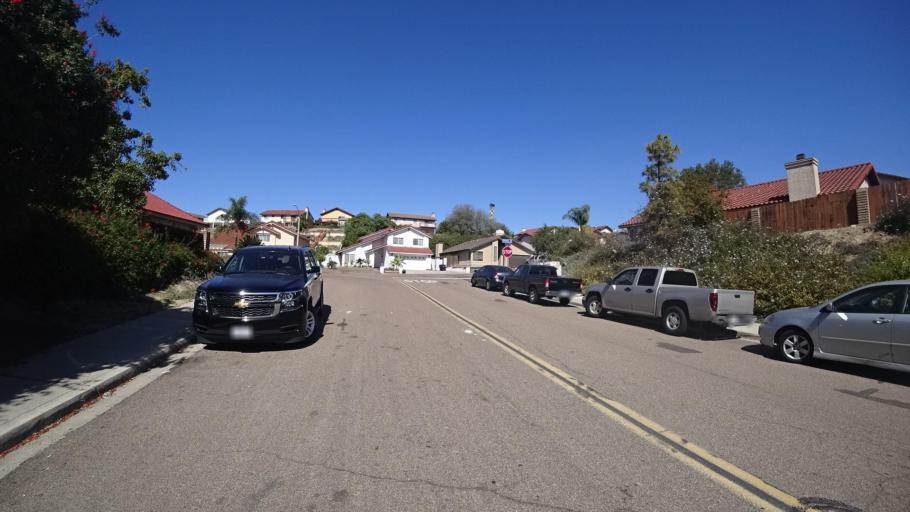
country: US
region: California
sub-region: San Diego County
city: Bonita
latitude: 32.6430
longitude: -117.0463
